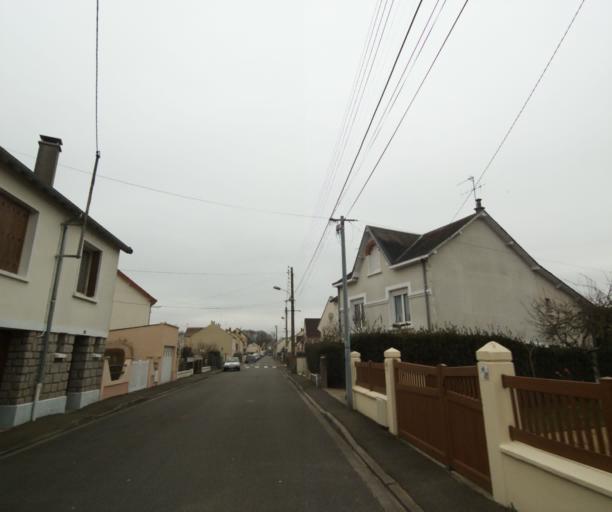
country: FR
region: Pays de la Loire
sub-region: Departement de la Sarthe
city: Le Mans
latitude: 47.9863
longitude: 0.1923
